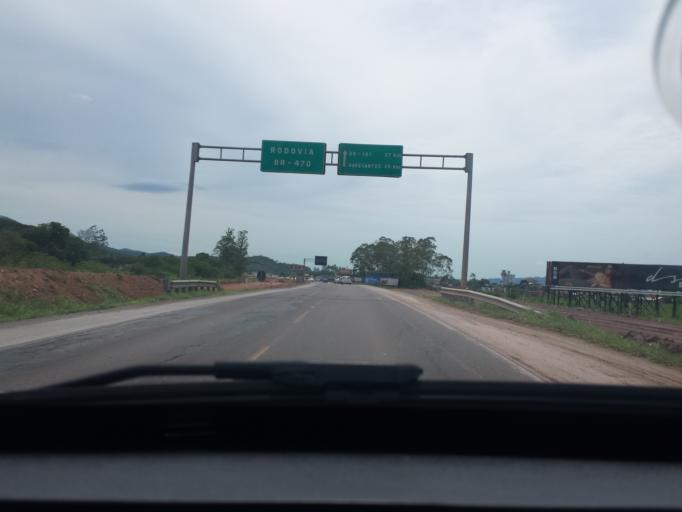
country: BR
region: Santa Catarina
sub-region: Gaspar
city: Gaspar
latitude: -26.9124
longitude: -48.9557
